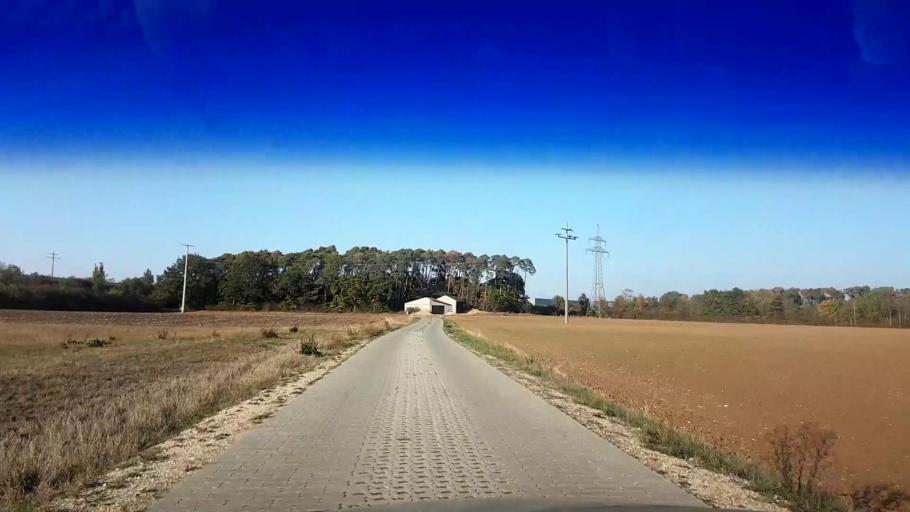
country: DE
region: Bavaria
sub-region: Upper Franconia
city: Strullendorf
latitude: 49.8386
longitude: 10.9509
